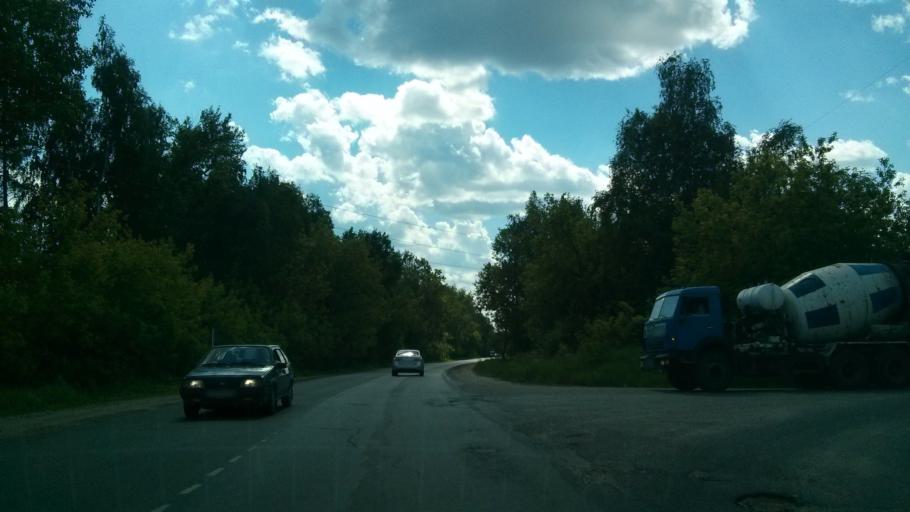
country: RU
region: Vladimir
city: Murom
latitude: 55.5491
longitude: 41.9981
